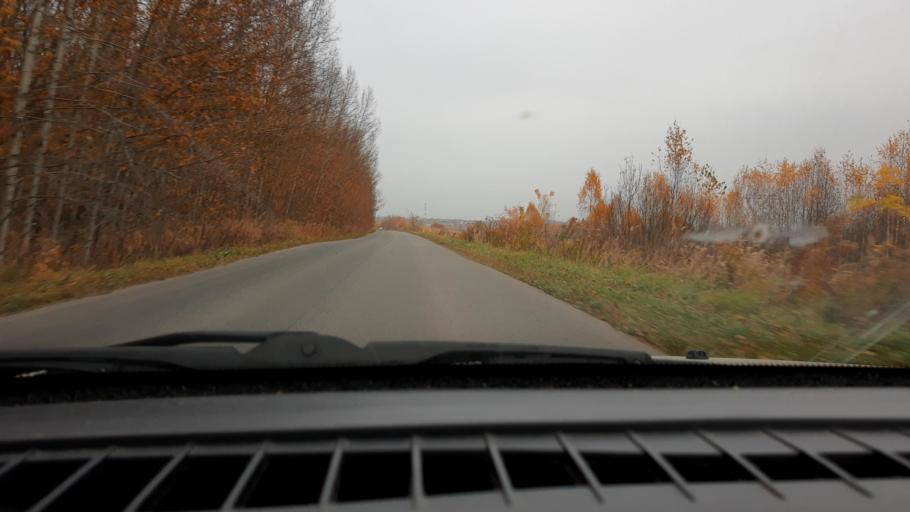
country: RU
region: Nizjnij Novgorod
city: Burevestnik
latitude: 56.0434
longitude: 43.8508
